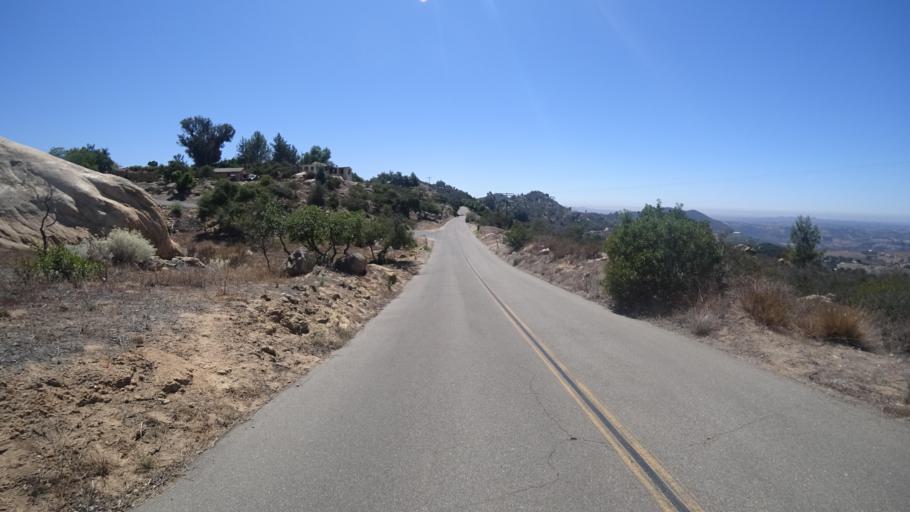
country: US
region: California
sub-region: San Diego County
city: Rainbow
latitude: 33.3964
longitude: -117.1300
